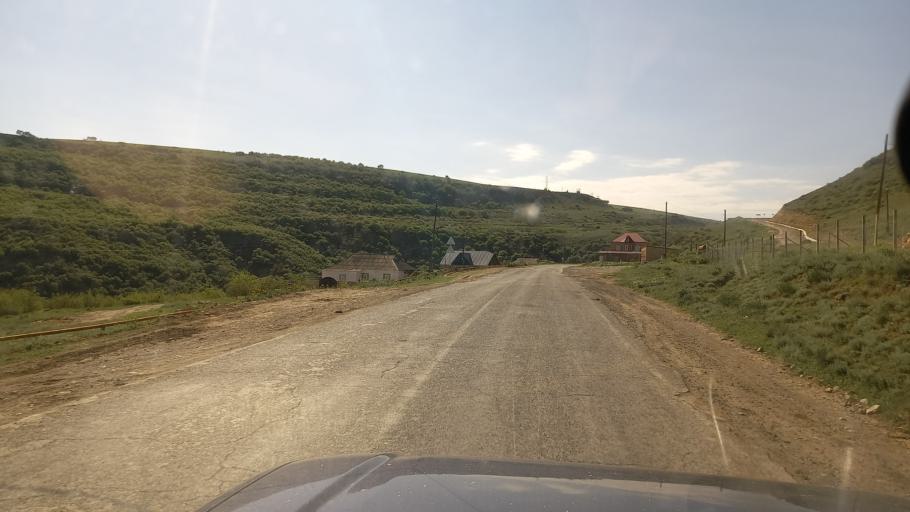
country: RU
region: Dagestan
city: Chinar
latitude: 41.9550
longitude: 48.1333
